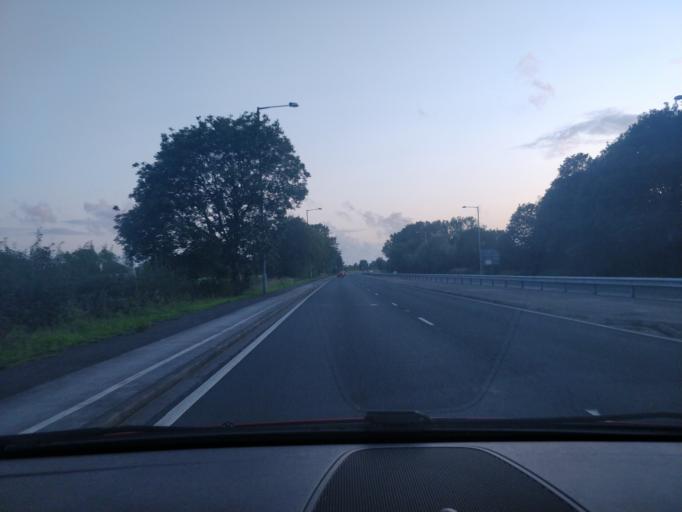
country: GB
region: England
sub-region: Lancashire
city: Croston
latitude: 53.7122
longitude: -2.7793
